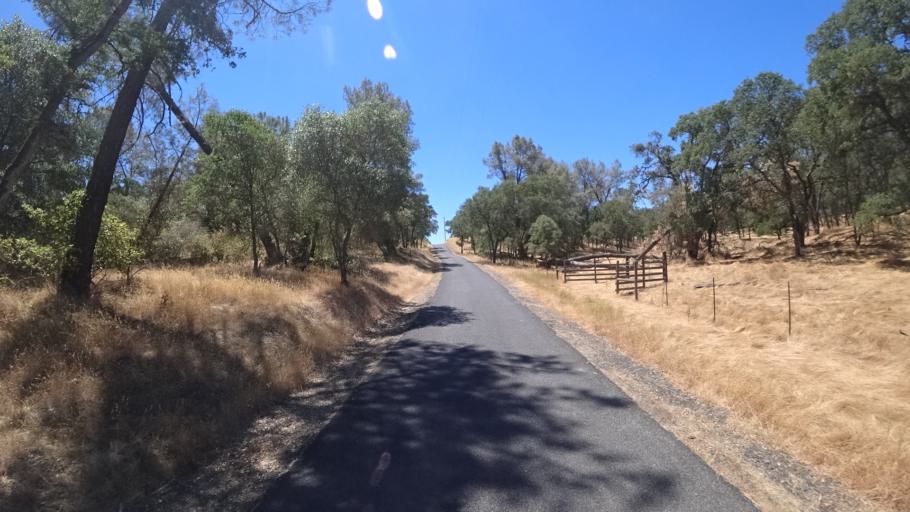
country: US
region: California
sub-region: Calaveras County
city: Copperopolis
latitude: 37.9764
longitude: -120.7018
